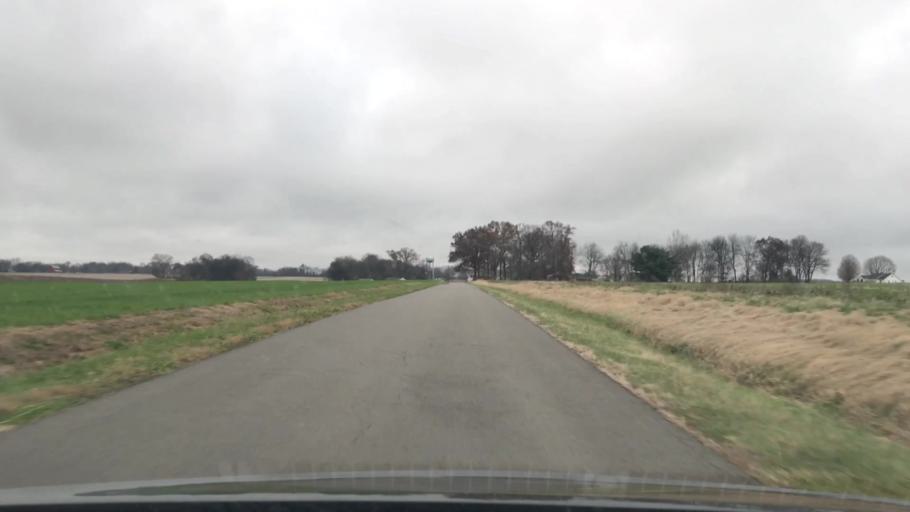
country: US
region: Kentucky
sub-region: Todd County
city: Elkton
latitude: 36.7871
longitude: -87.1512
